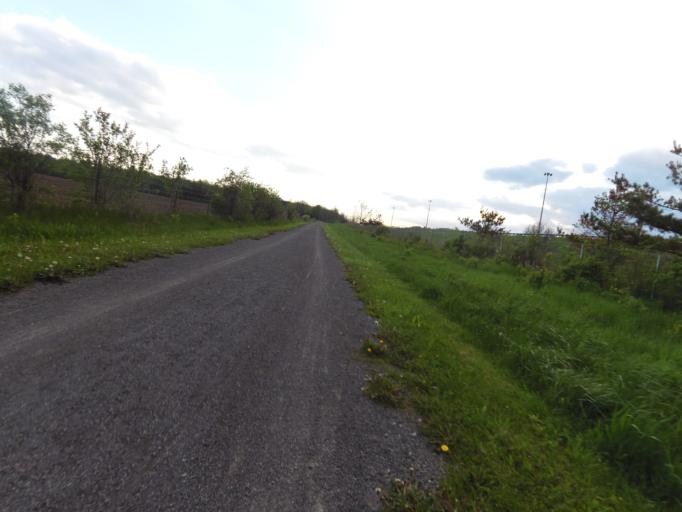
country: CA
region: Ontario
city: Bells Corners
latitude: 45.3311
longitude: -75.8573
